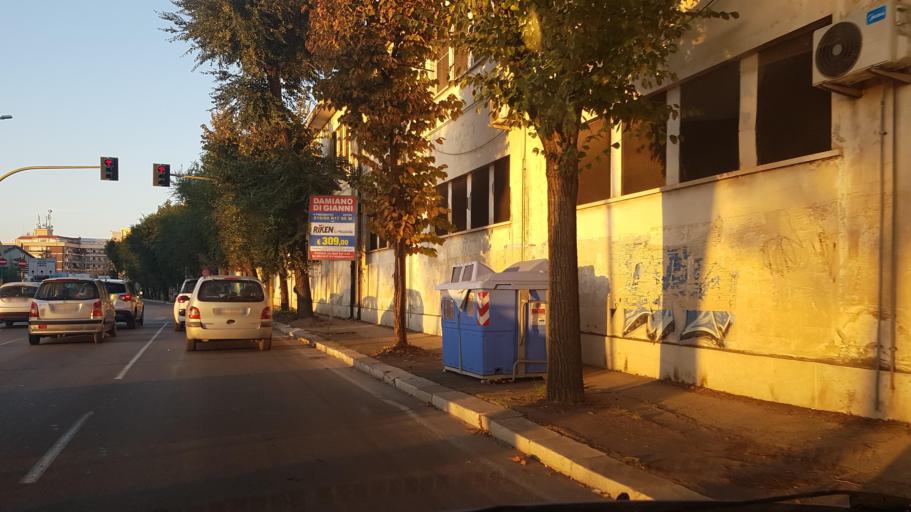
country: IT
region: Apulia
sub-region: Provincia di Foggia
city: Foggia
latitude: 41.4604
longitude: 15.5646
